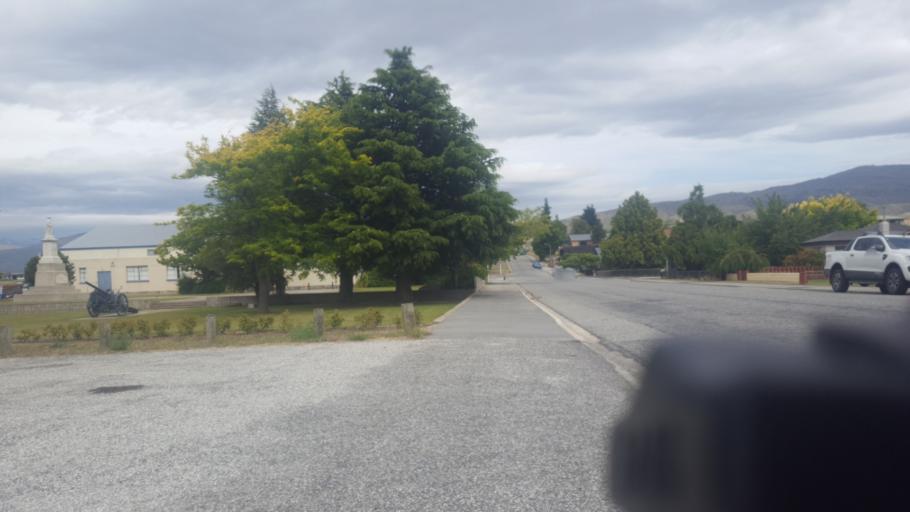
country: NZ
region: Otago
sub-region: Queenstown-Lakes District
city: Wanaka
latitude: -45.0488
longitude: 169.2043
